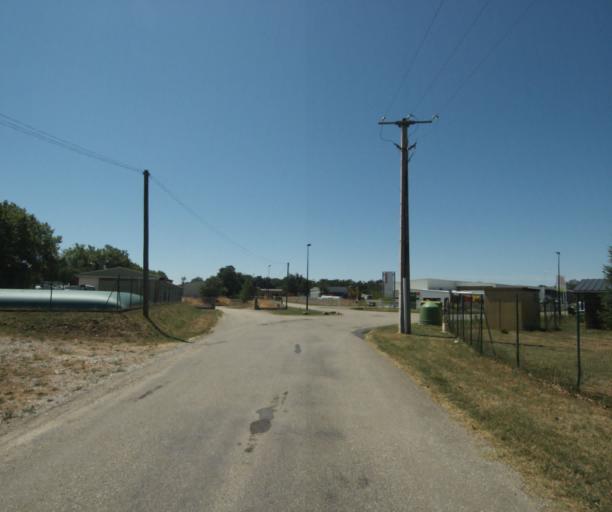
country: FR
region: Midi-Pyrenees
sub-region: Departement de la Haute-Garonne
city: Saint-Felix-Lauragais
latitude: 43.4454
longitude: 1.9448
